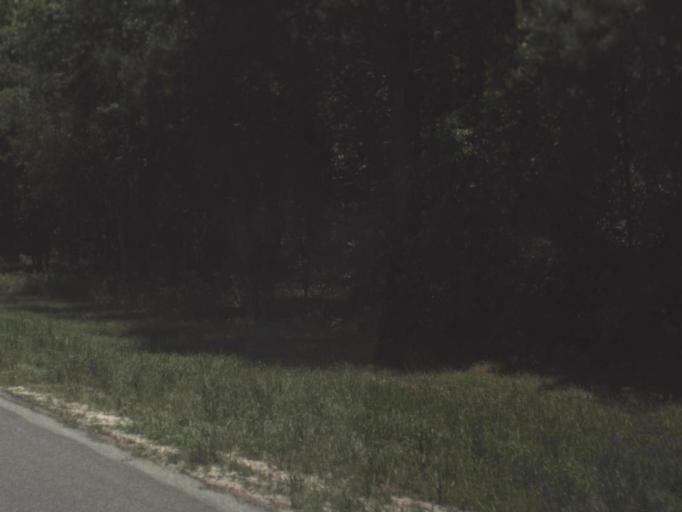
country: US
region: Florida
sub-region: Suwannee County
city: Live Oak
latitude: 30.3388
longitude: -83.0798
